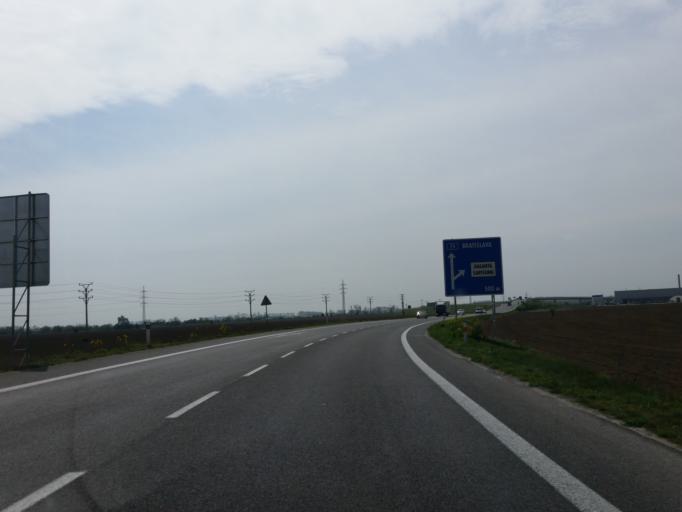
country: SK
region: Trnavsky
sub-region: Okres Galanta
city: Galanta
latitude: 48.1887
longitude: 17.7494
